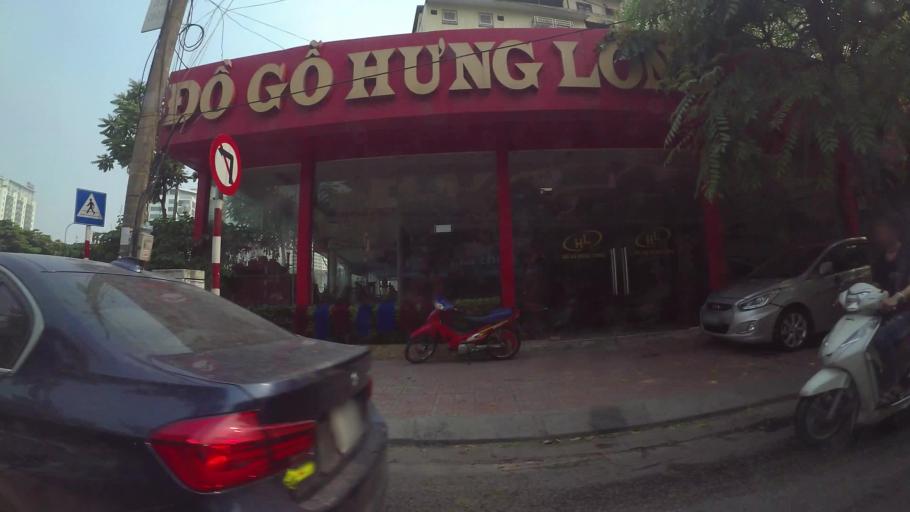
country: VN
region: Ha Noi
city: Cau Giay
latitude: 21.0275
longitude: 105.8125
